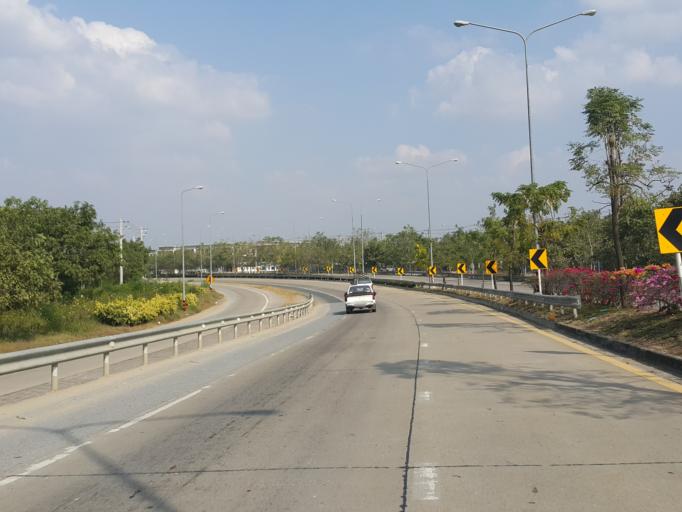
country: TH
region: Chiang Mai
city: Saraphi
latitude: 18.7533
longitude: 99.0341
